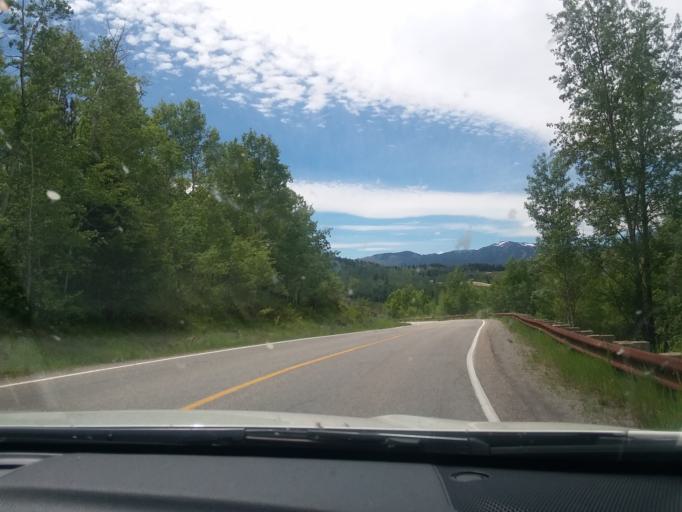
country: US
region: Wyoming
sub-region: Teton County
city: Jackson
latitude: 43.4940
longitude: -110.7829
